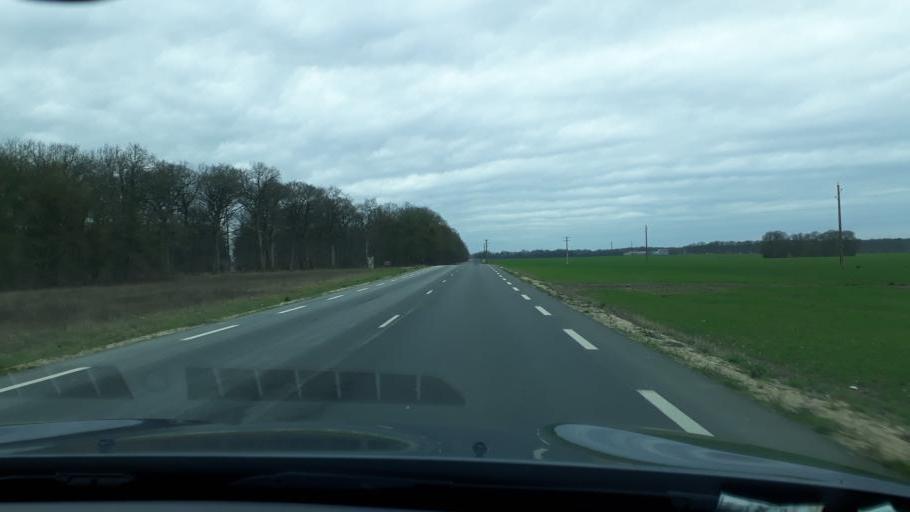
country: FR
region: Centre
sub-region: Departement du Loiret
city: Chanteau
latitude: 48.0254
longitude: 1.9694
